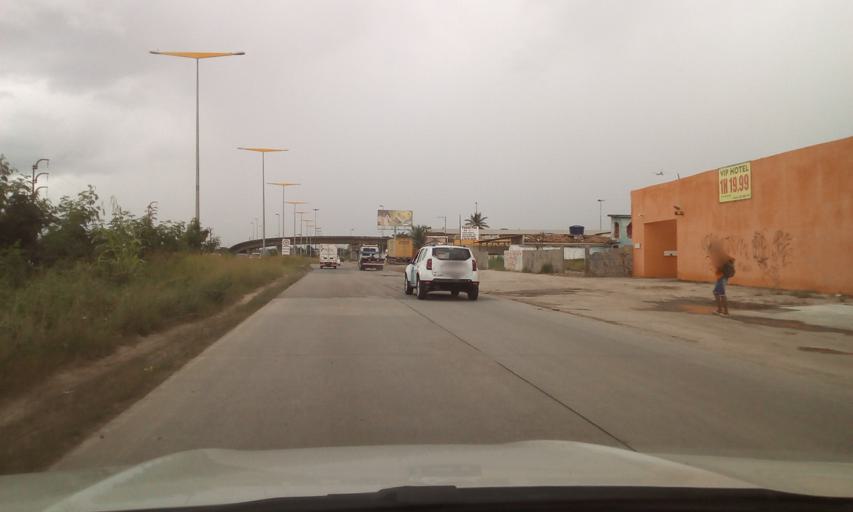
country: BR
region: Pernambuco
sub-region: Recife
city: Recife
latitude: -8.0727
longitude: -34.9383
